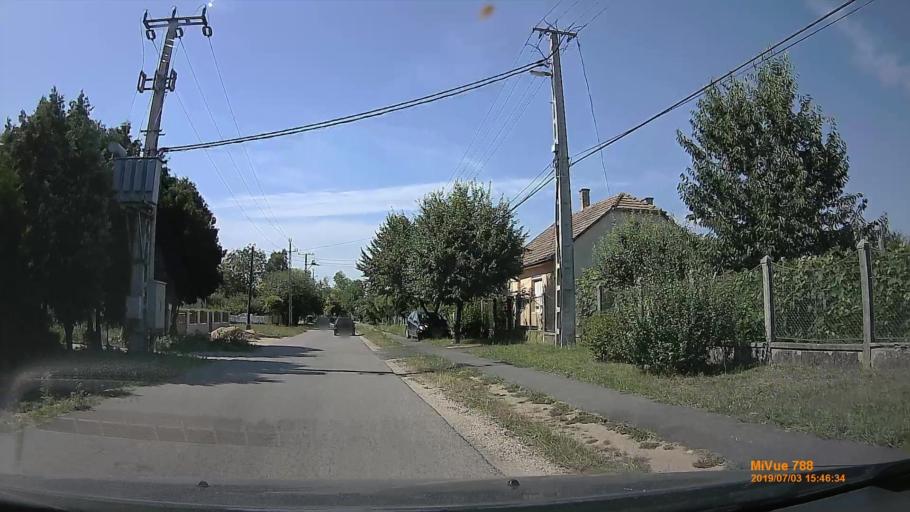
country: HU
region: Gyor-Moson-Sopron
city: Toltestava
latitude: 47.6911
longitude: 17.7483
